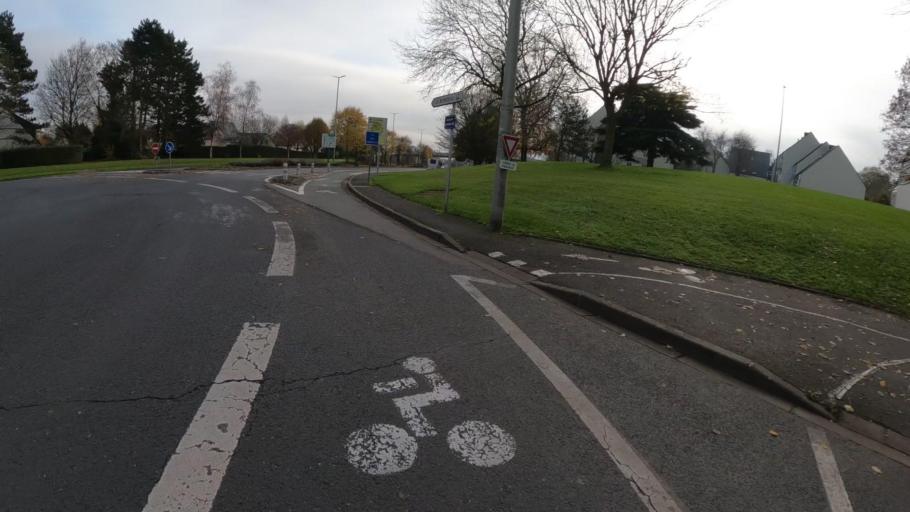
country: FR
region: Lower Normandy
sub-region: Departement du Calvados
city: Epron
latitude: 49.2061
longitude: -0.3769
